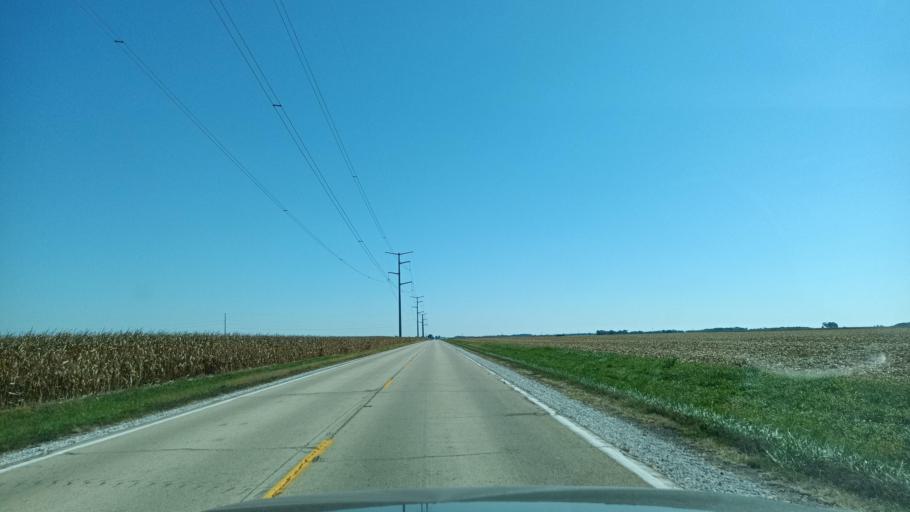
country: US
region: Illinois
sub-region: Peoria County
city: Elmwood
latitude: 40.9023
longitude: -89.9852
